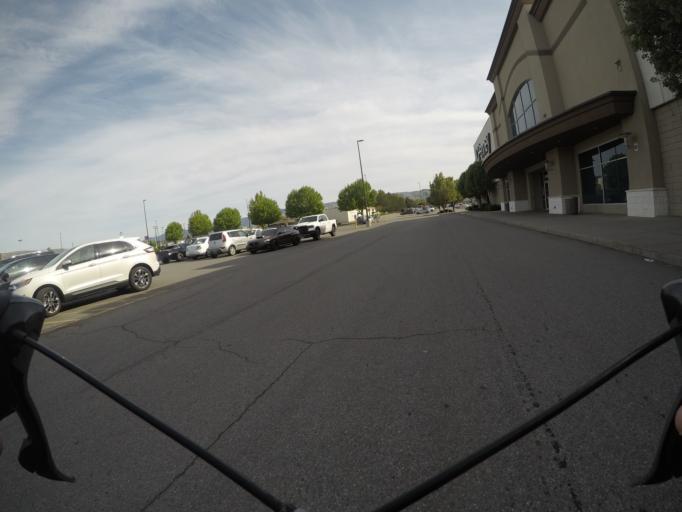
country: US
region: Washington
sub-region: Chelan County
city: Wenatchee
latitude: 47.4398
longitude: -120.3270
